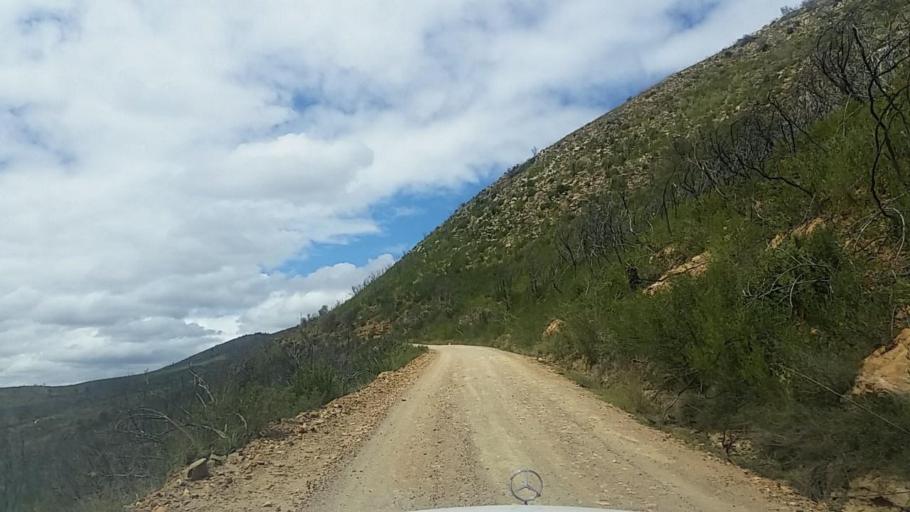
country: ZA
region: Western Cape
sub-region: Eden District Municipality
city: Knysna
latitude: -33.8205
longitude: 23.1764
